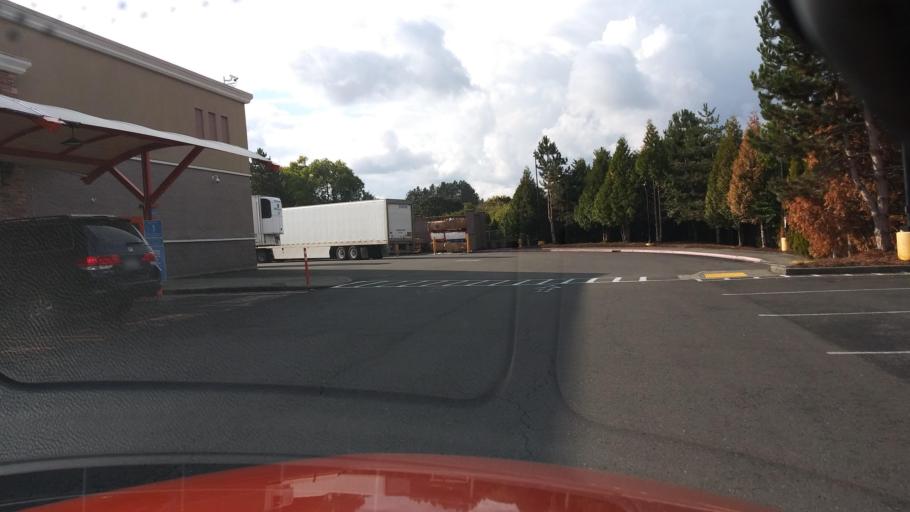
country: US
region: Oregon
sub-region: Washington County
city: Cornelius
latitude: 45.5230
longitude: -123.0698
